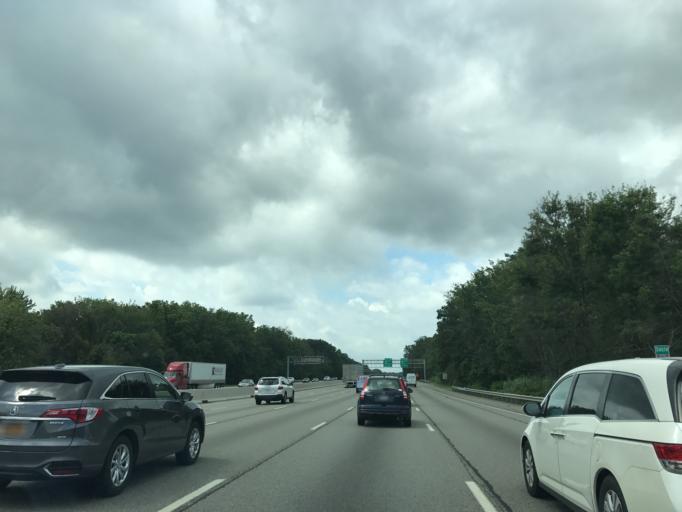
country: US
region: New Jersey
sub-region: Morris County
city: Parsippany
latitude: 40.8434
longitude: -74.4309
